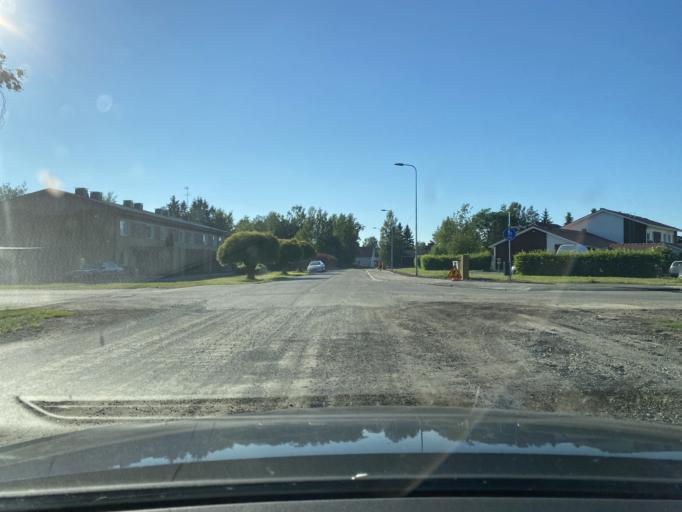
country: FI
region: Satakunta
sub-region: Pori
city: Huittinen
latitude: 61.1694
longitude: 22.7012
